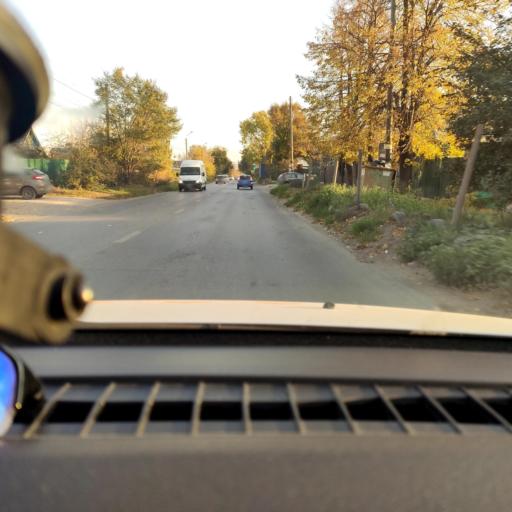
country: RU
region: Samara
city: Samara
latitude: 53.1774
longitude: 50.1692
